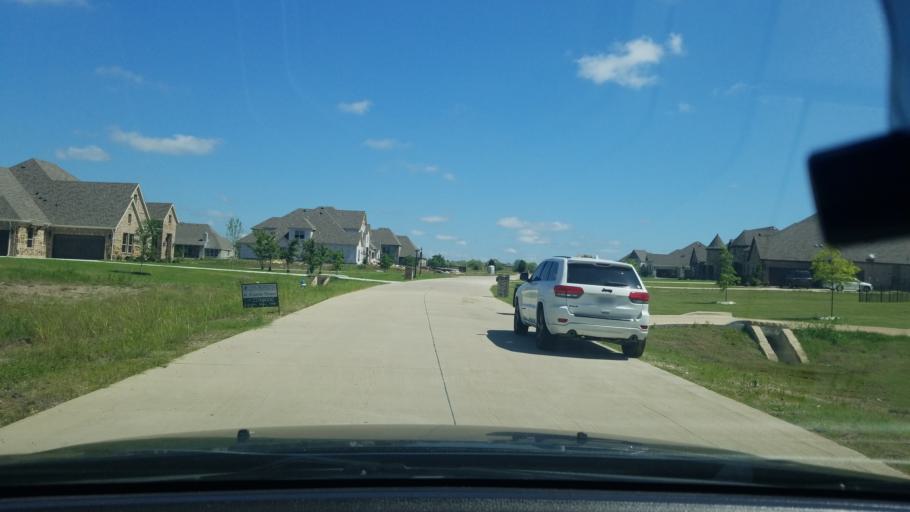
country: US
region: Texas
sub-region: Dallas County
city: Sunnyvale
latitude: 32.8003
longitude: -96.5706
